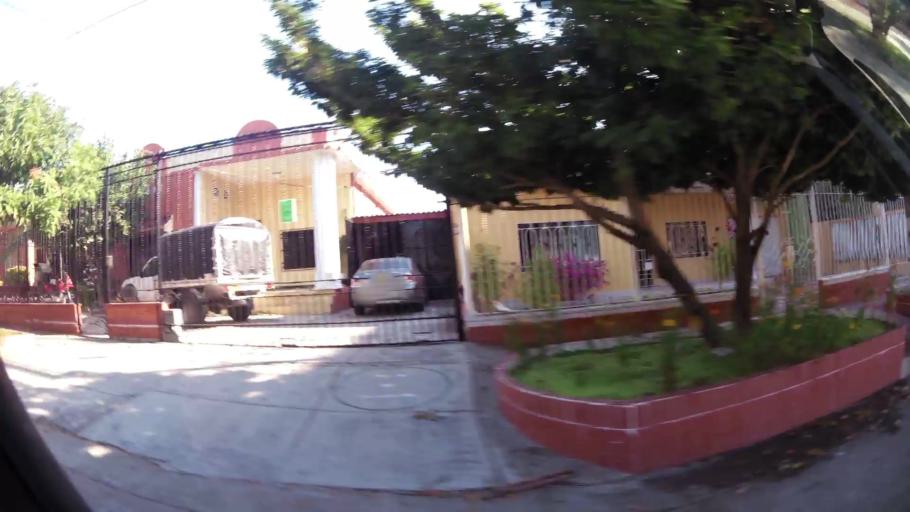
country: CO
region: Atlantico
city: Barranquilla
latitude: 11.0030
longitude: -74.7974
